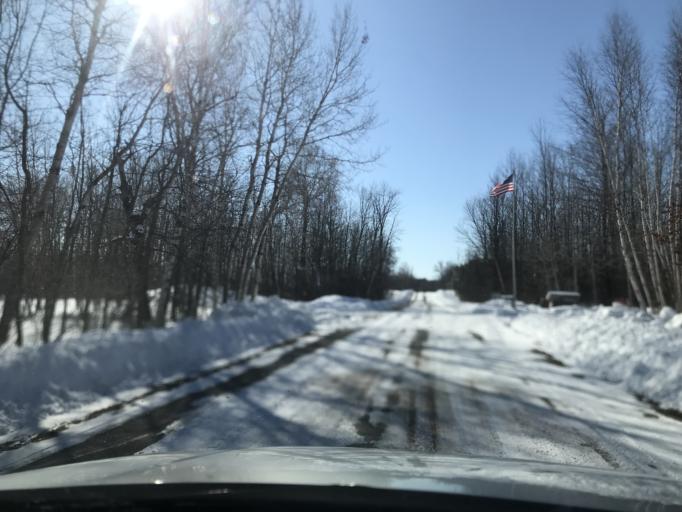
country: US
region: Wisconsin
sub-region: Marinette County
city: Peshtigo
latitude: 45.1748
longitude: -87.7639
